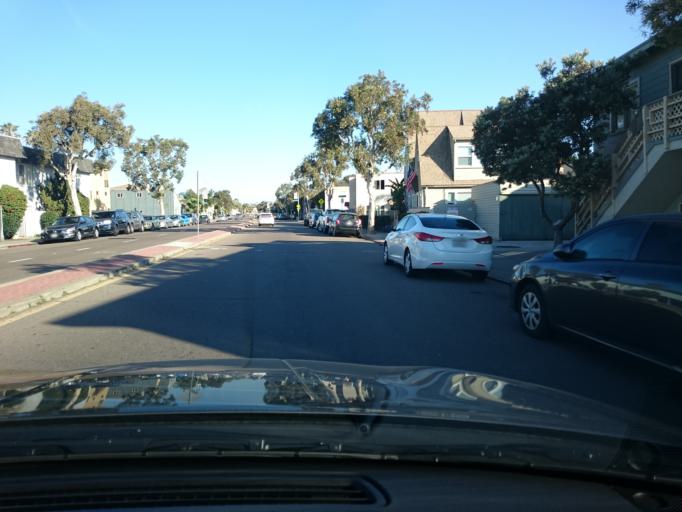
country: US
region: California
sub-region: San Diego County
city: La Jolla
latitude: 32.7732
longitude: -117.2514
